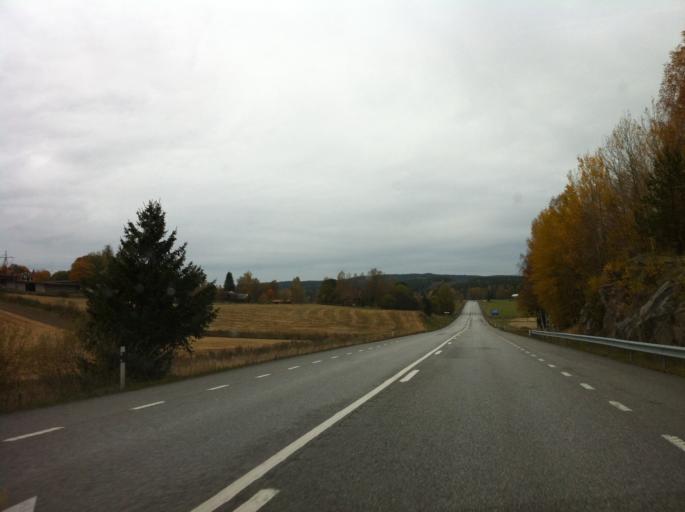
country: SE
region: OErebro
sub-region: Lindesbergs Kommun
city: Stora
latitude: 59.7890
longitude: 15.1530
